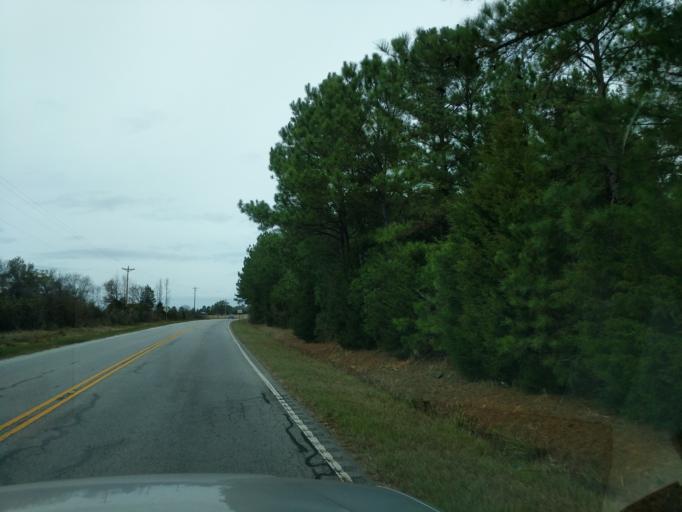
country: US
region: South Carolina
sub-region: Saluda County
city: Saluda
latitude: 34.0372
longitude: -81.7697
